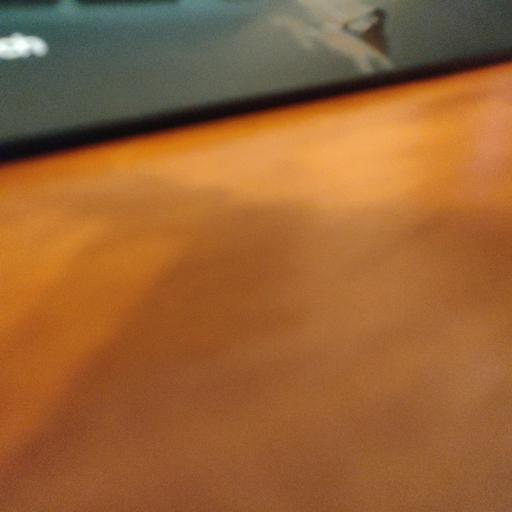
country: SE
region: Vaestmanland
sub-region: Vasteras
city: Tillberga
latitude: 59.6953
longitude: 16.6752
